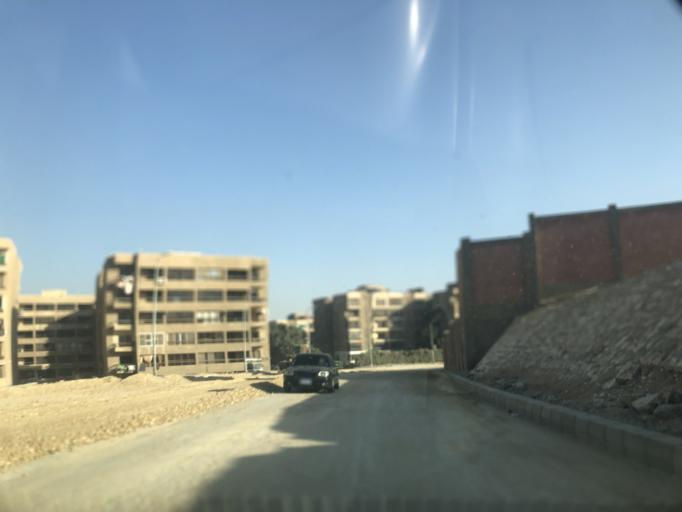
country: EG
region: Al Jizah
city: Al Jizah
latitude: 29.9868
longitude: 31.1124
